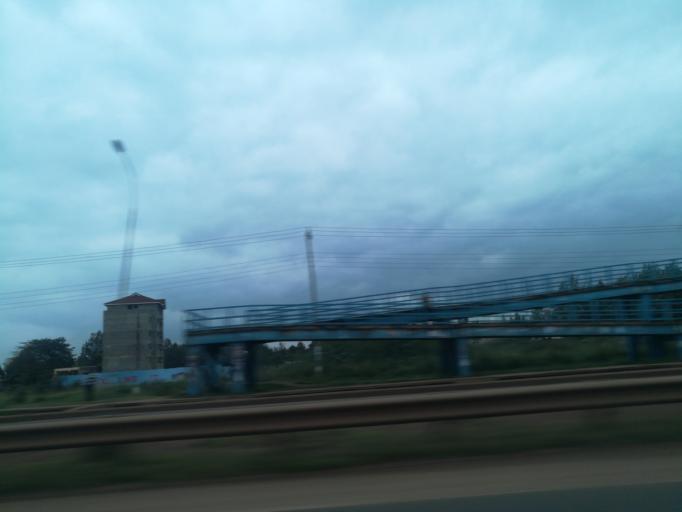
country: KE
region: Nairobi Area
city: Thika
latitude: -1.0999
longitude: 37.0230
